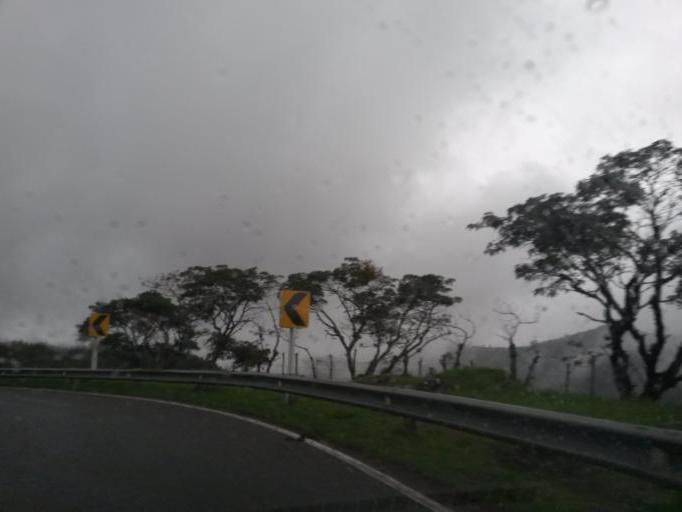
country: CO
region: Cauca
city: Popayan
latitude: 2.4058
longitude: -76.5056
